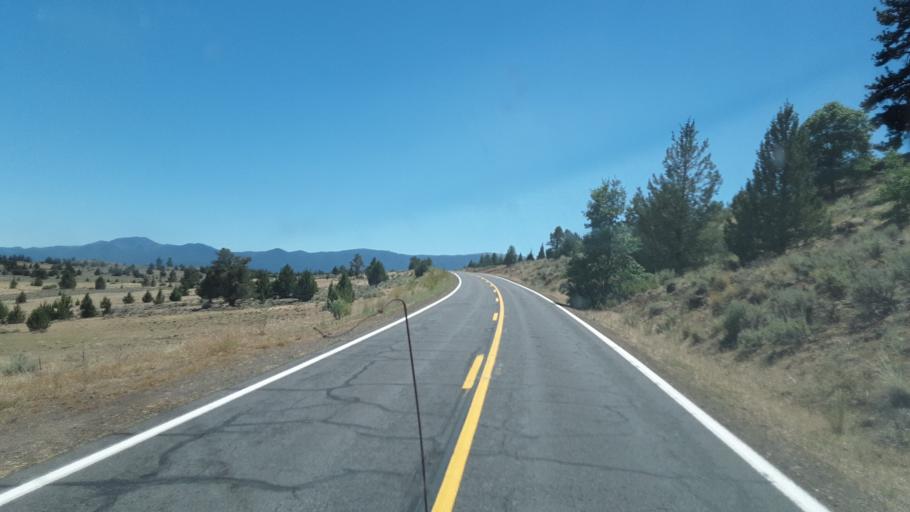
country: US
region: California
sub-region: Lassen County
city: Susanville
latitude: 40.4545
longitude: -120.6214
